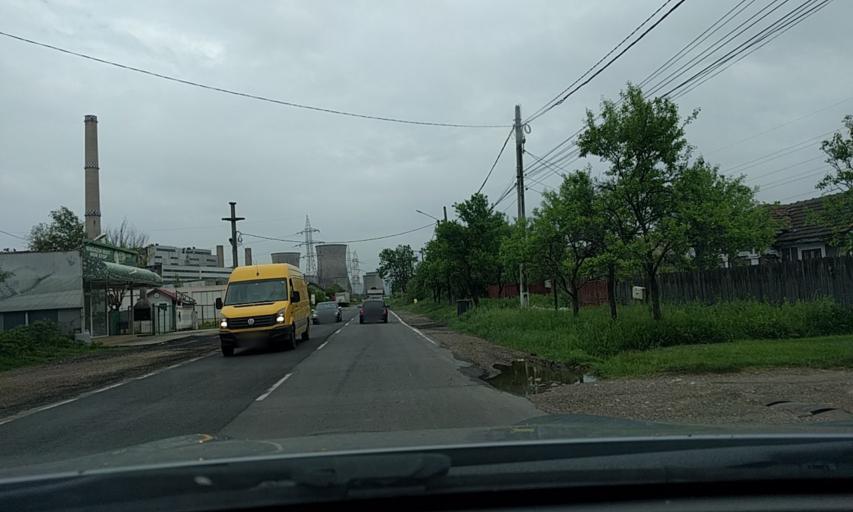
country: RO
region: Dambovita
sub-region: Comuna Doicesti
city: Doicesti
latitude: 44.9965
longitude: 25.4035
